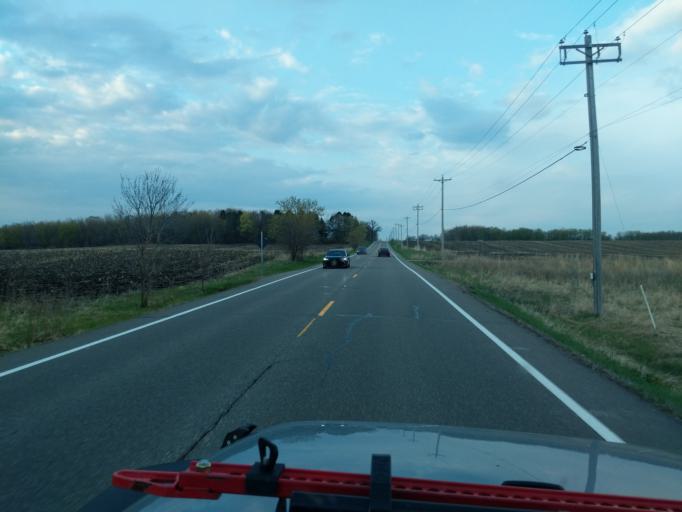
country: US
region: Minnesota
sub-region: Hennepin County
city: Rogers
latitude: 45.1520
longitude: -93.5219
